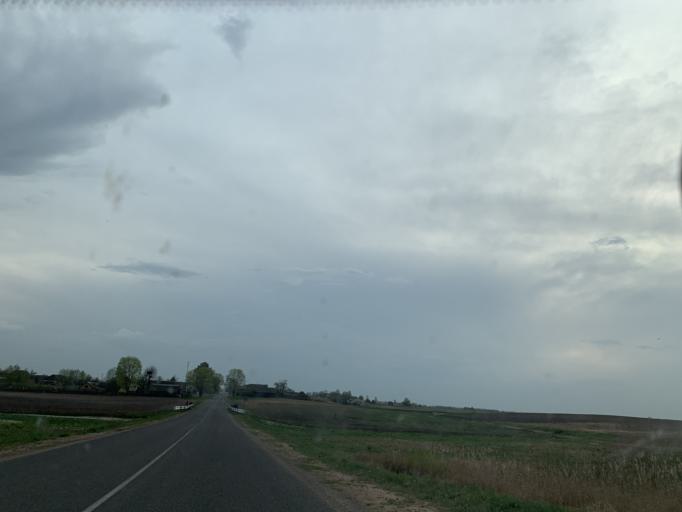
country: BY
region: Minsk
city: Kapyl'
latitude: 53.2871
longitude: 26.9868
